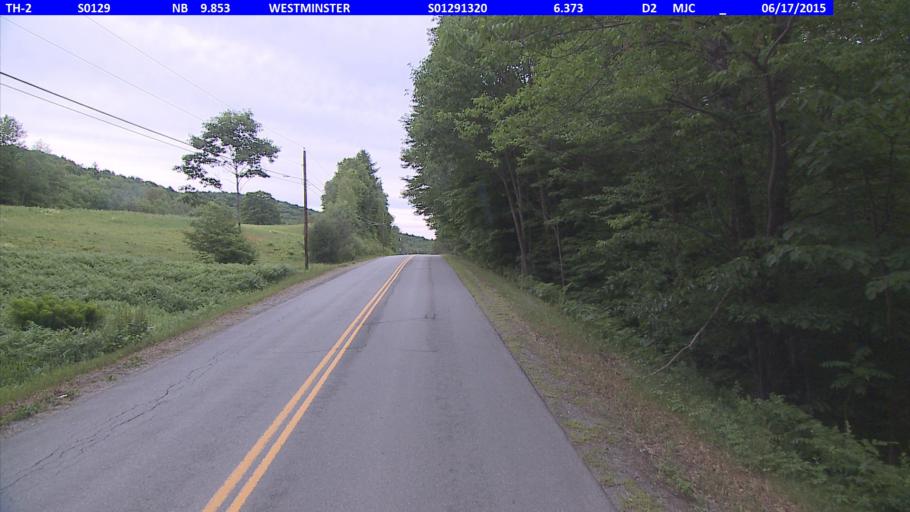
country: US
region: Vermont
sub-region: Windham County
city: Rockingham
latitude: 43.1063
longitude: -72.5380
